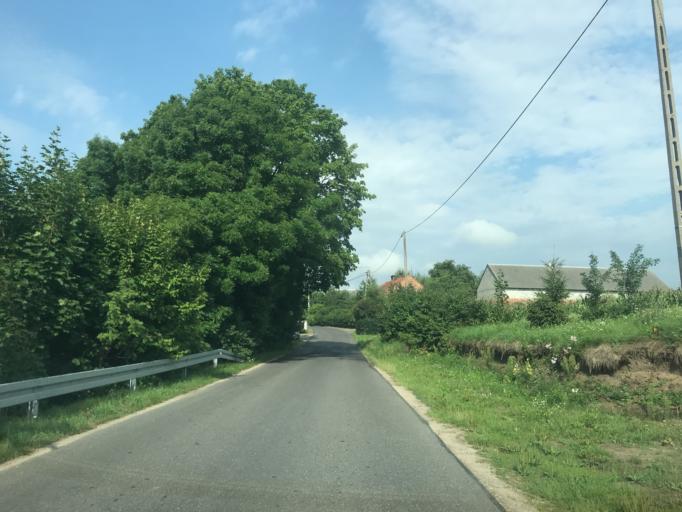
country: PL
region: Warmian-Masurian Voivodeship
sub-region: Powiat nowomiejski
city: Kurzetnik
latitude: 53.3717
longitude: 19.5613
